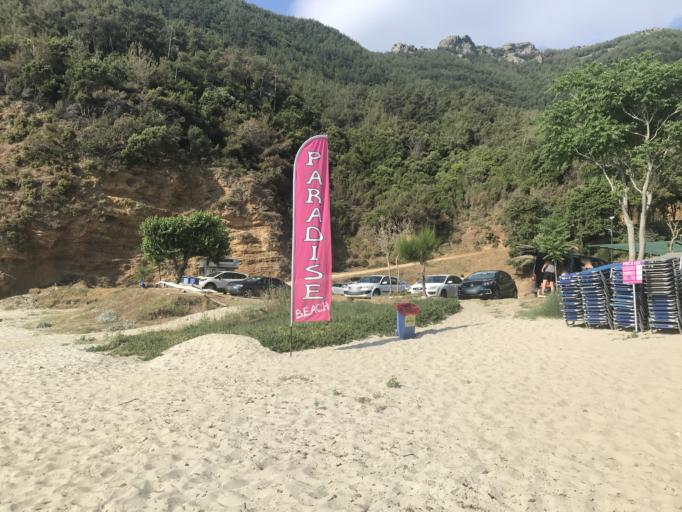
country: GR
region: East Macedonia and Thrace
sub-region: Nomos Kavalas
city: Potamia
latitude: 40.6446
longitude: 24.7673
